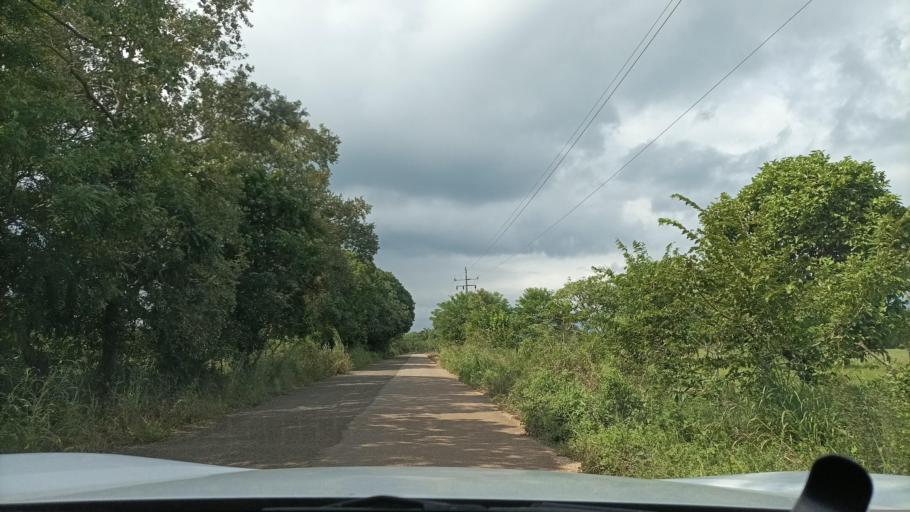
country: MX
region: Veracruz
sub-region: Chinameca
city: Chacalapa
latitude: 18.0823
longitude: -94.6778
